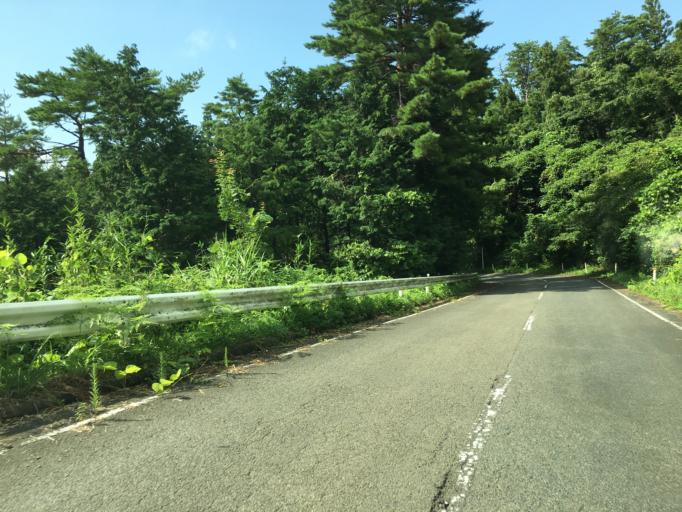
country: JP
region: Miyagi
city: Marumori
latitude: 37.8849
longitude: 140.8536
